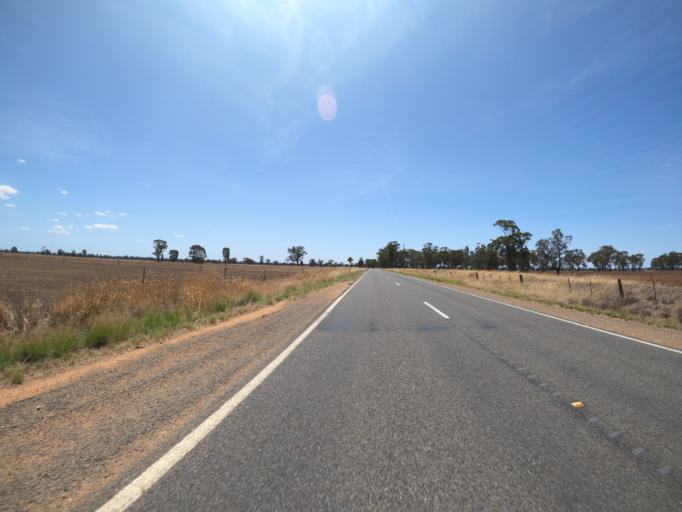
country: AU
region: Victoria
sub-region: Moira
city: Yarrawonga
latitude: -36.2012
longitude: 145.9672
